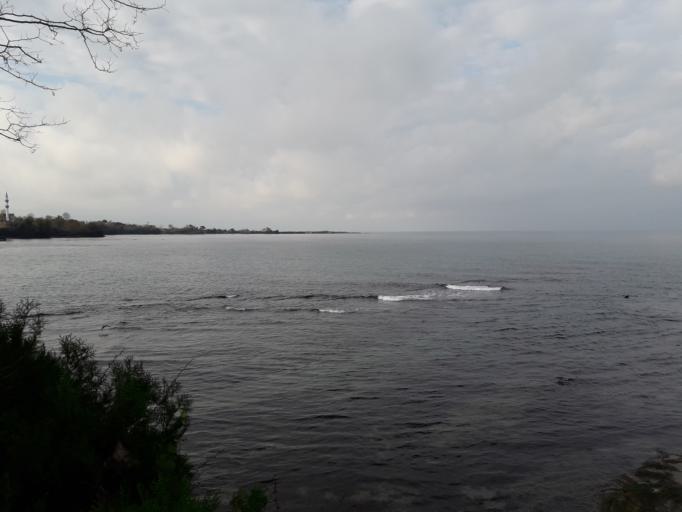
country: TR
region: Ordu
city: Persembe
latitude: 41.1264
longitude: 37.6922
